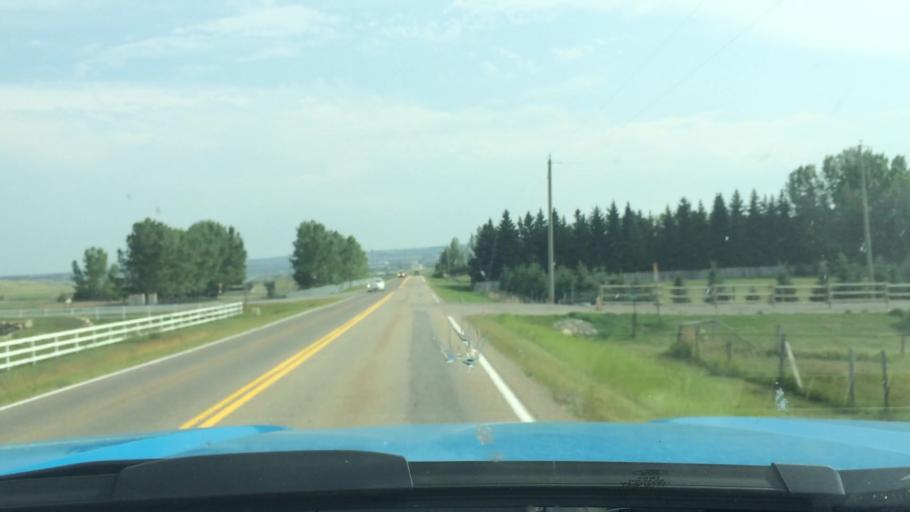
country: CA
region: Alberta
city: Airdrie
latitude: 51.2018
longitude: -114.1413
